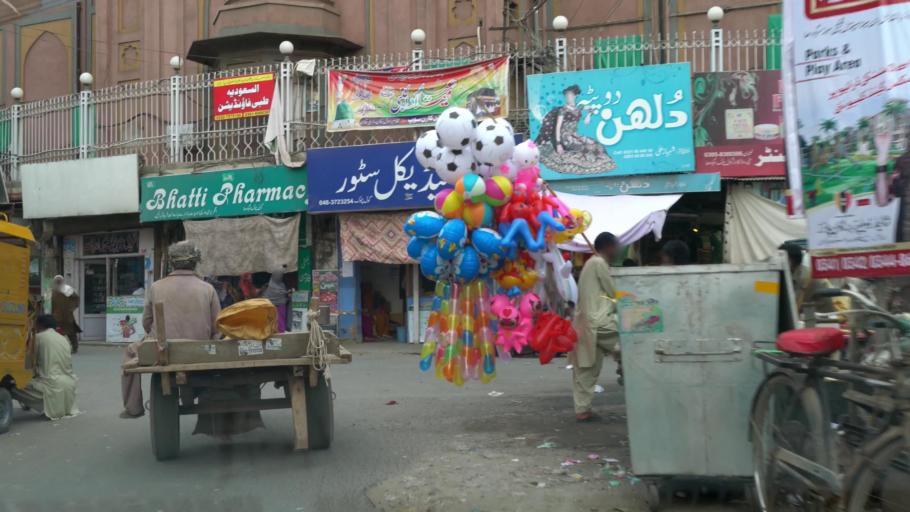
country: PK
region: Punjab
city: Sargodha
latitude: 32.0865
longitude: 72.6621
